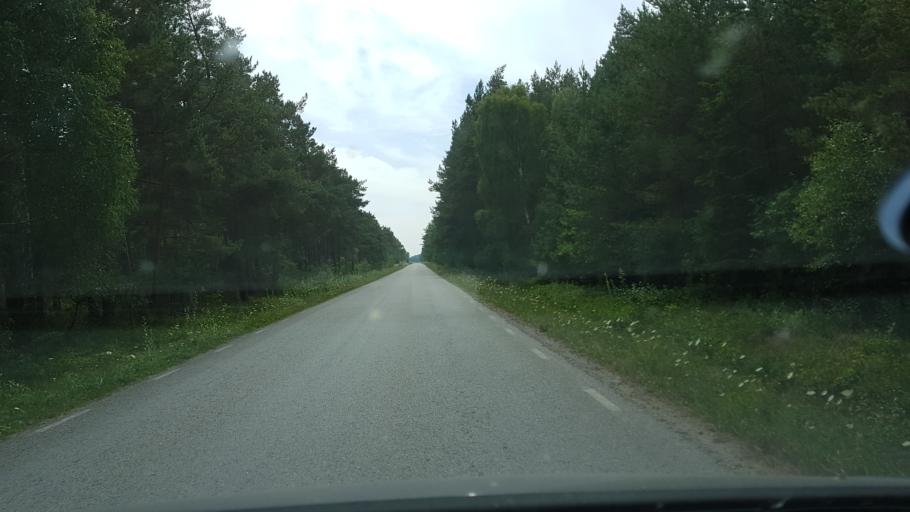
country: SE
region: Gotland
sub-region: Gotland
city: Visby
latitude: 57.7168
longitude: 18.5095
